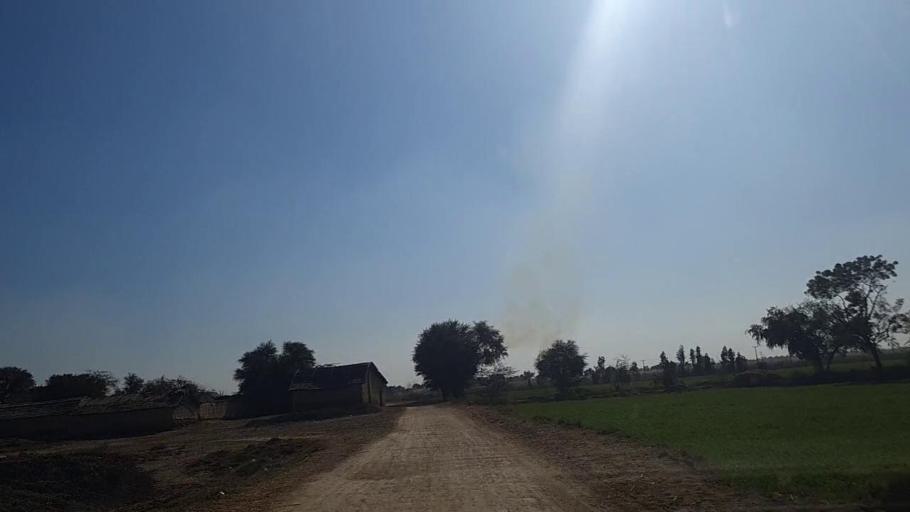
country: PK
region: Sindh
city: Sakrand
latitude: 26.2514
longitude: 68.1925
